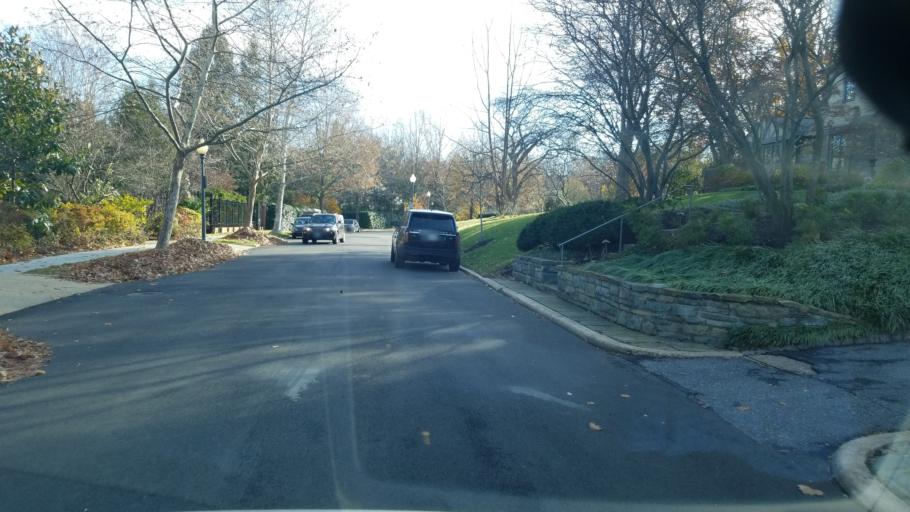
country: US
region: Maryland
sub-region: Montgomery County
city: Brookmont
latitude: 38.9345
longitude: -77.0962
